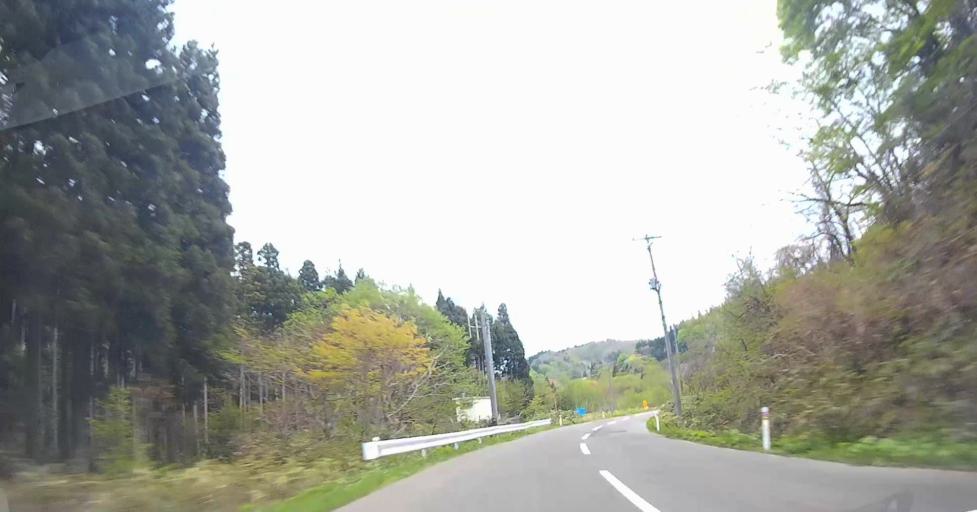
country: JP
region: Aomori
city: Goshogawara
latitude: 41.1209
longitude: 140.5233
